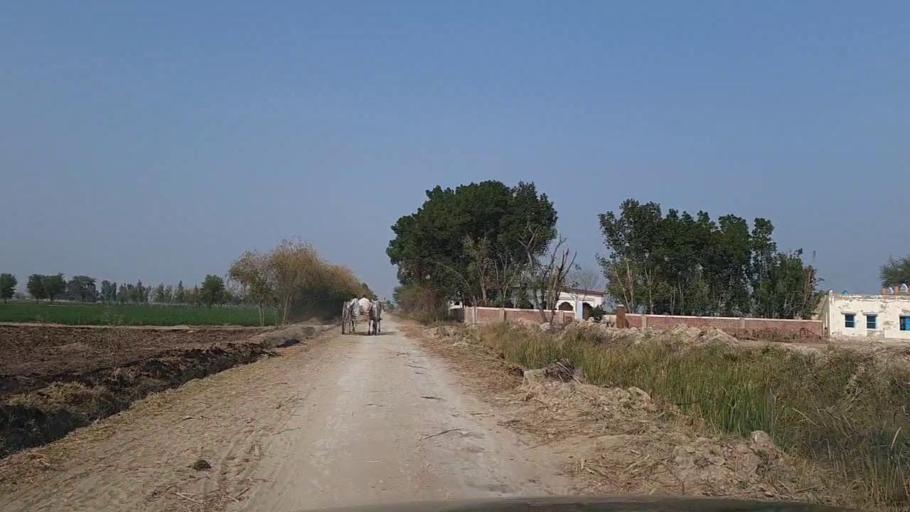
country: PK
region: Sindh
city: Daur
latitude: 26.3978
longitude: 68.4238
